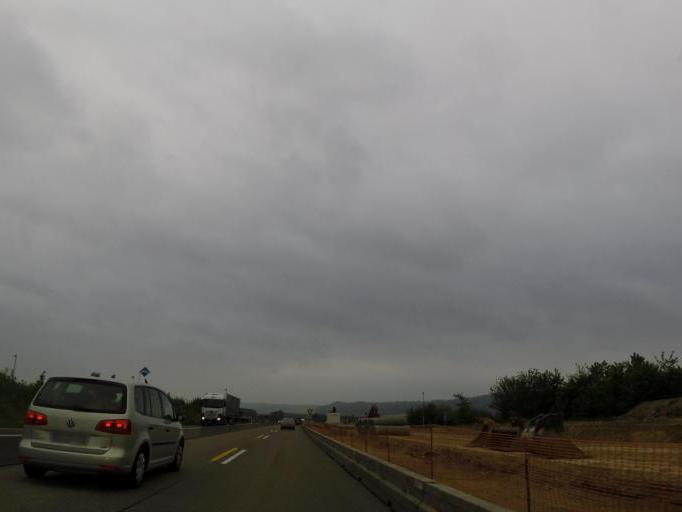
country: DE
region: Lower Saxony
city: Seesen
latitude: 51.9260
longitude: 10.1420
